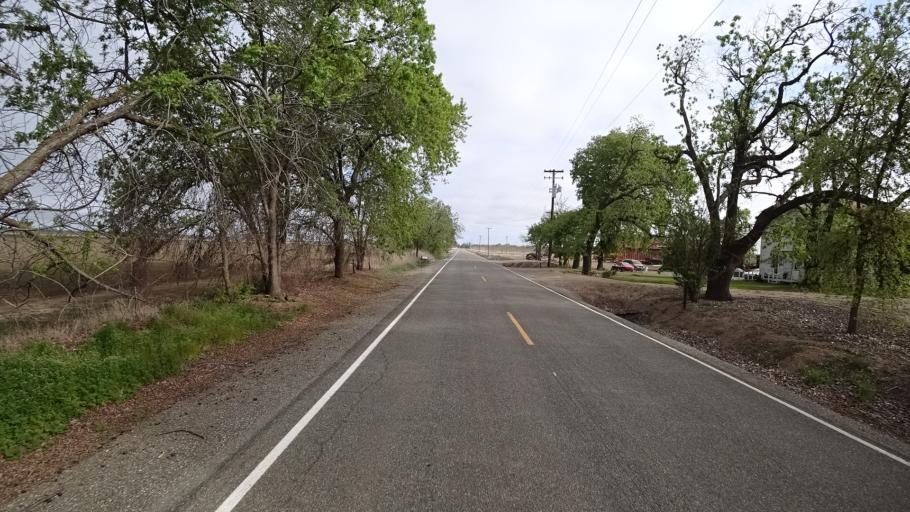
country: US
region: California
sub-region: Colusa County
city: Colusa
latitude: 39.4066
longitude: -121.9667
